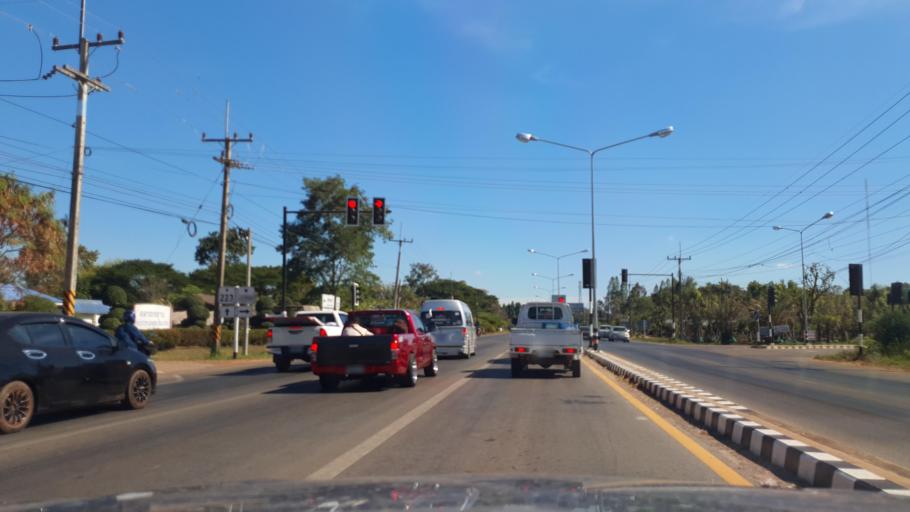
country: TH
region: Sakon Nakhon
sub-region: Amphoe Khok Si Suphan
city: Khok Si Suphan
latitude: 17.0700
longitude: 104.2148
